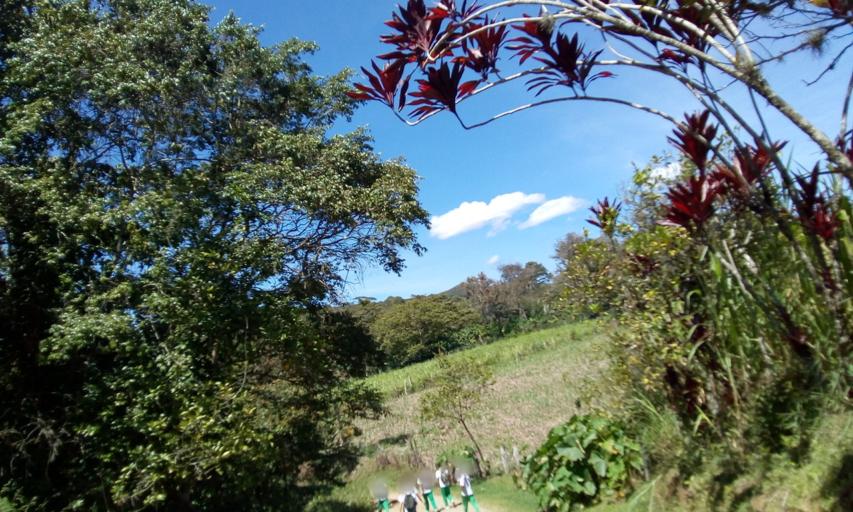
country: CO
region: Santander
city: Guepsa
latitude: 6.0073
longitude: -73.5481
